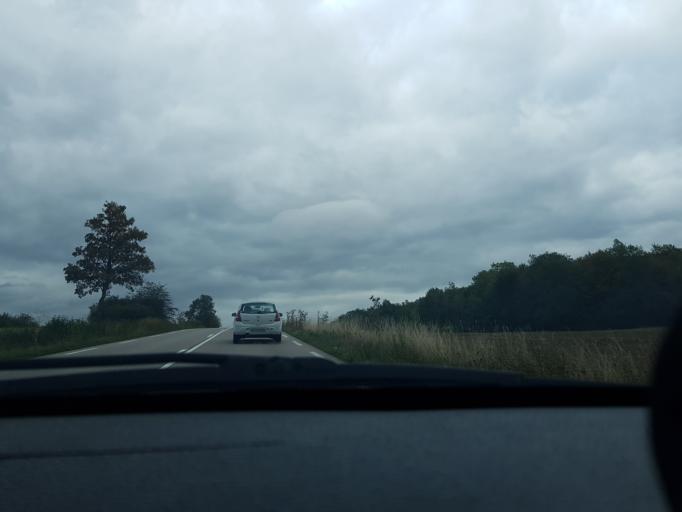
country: FR
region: Lorraine
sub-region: Departement de la Moselle
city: Chateau-Salins
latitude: 48.7685
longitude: 6.4408
